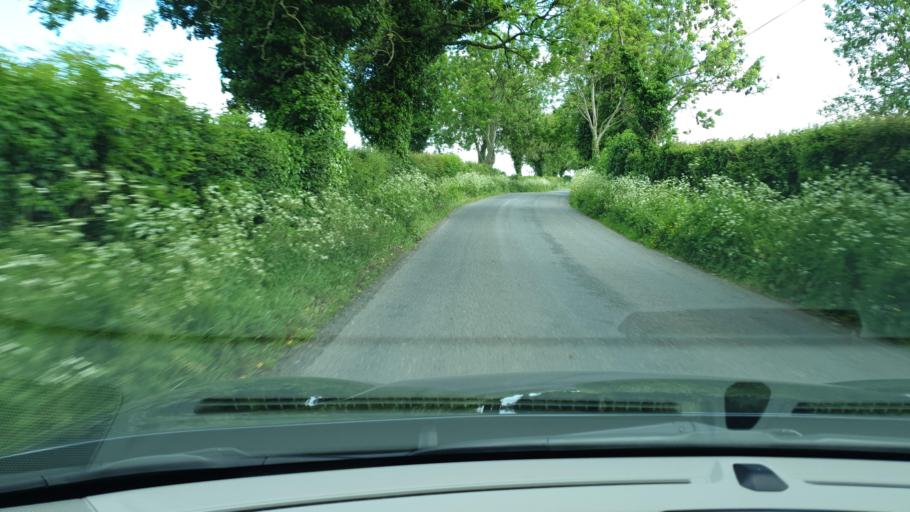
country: IE
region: Leinster
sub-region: An Mhi
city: Navan
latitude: 53.7936
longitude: -6.6873
